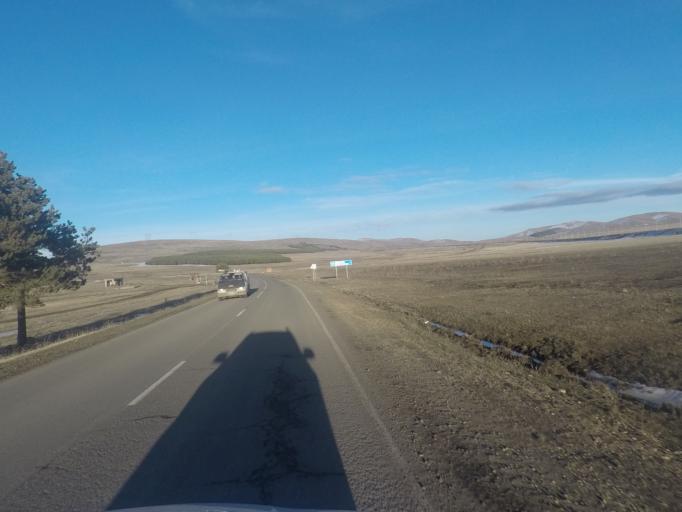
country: GE
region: Kvemo Kartli
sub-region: Tsalka
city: Tsalka
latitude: 41.6188
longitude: 44.1381
